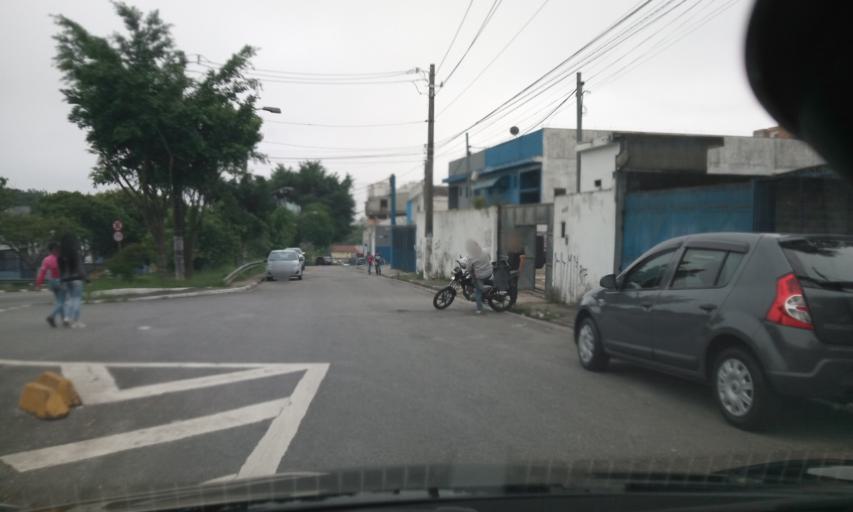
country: BR
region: Sao Paulo
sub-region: Sao Bernardo Do Campo
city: Sao Bernardo do Campo
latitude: -23.7028
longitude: -46.5628
